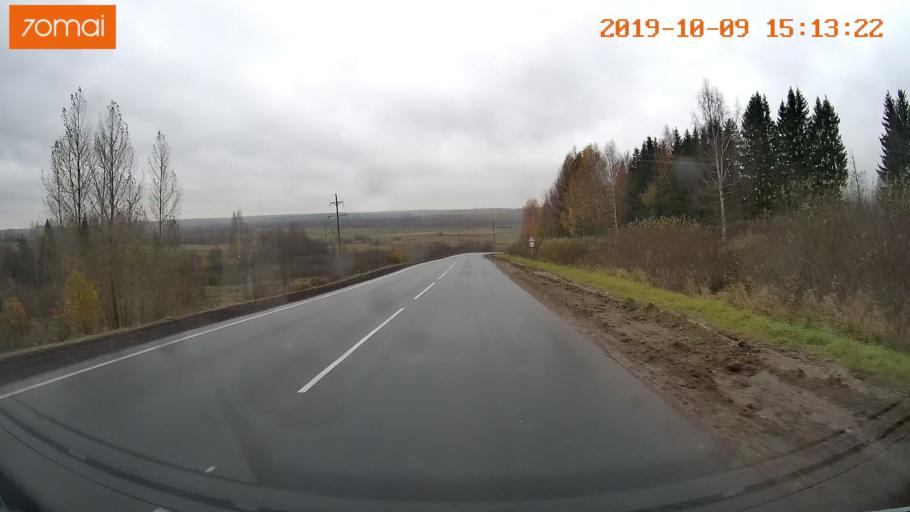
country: RU
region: Kostroma
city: Susanino
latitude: 58.1468
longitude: 41.6152
